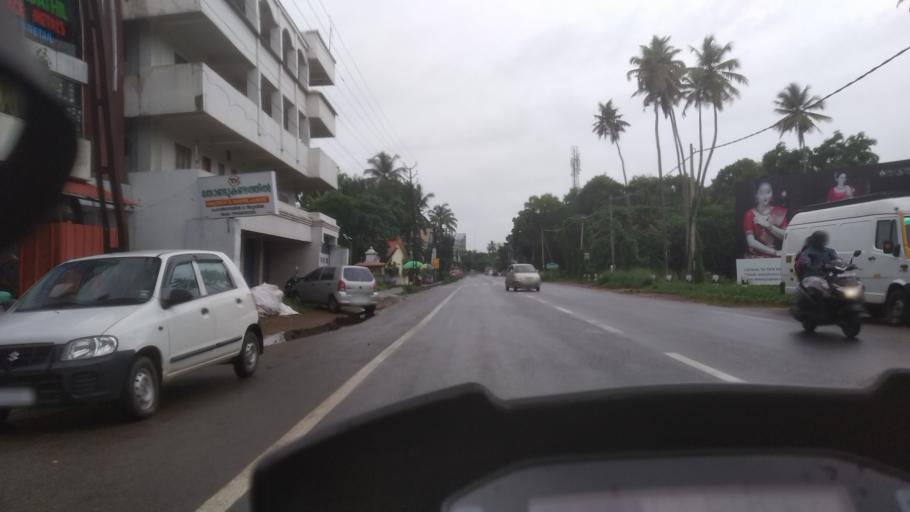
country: IN
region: Kerala
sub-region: Alappuzha
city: Kayankulam
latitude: 9.1355
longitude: 76.5132
